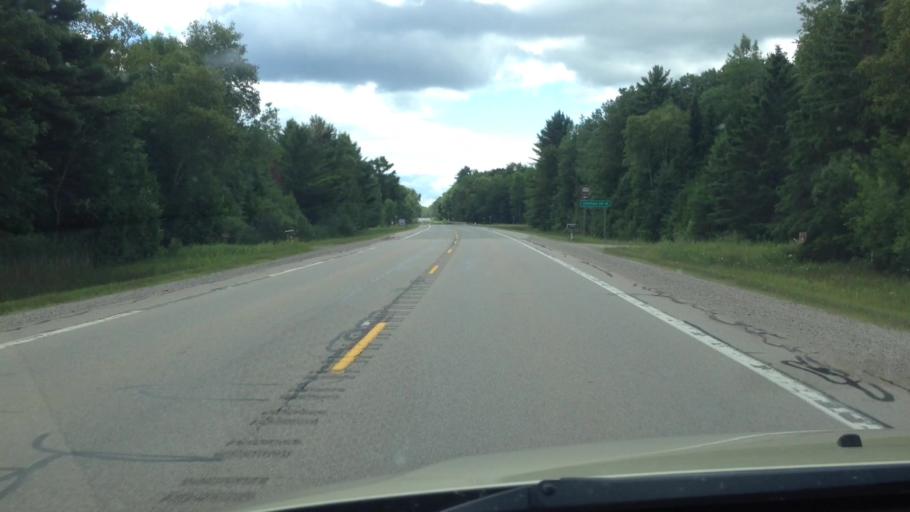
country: US
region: Michigan
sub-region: Menominee County
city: Menominee
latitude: 45.3232
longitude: -87.4291
